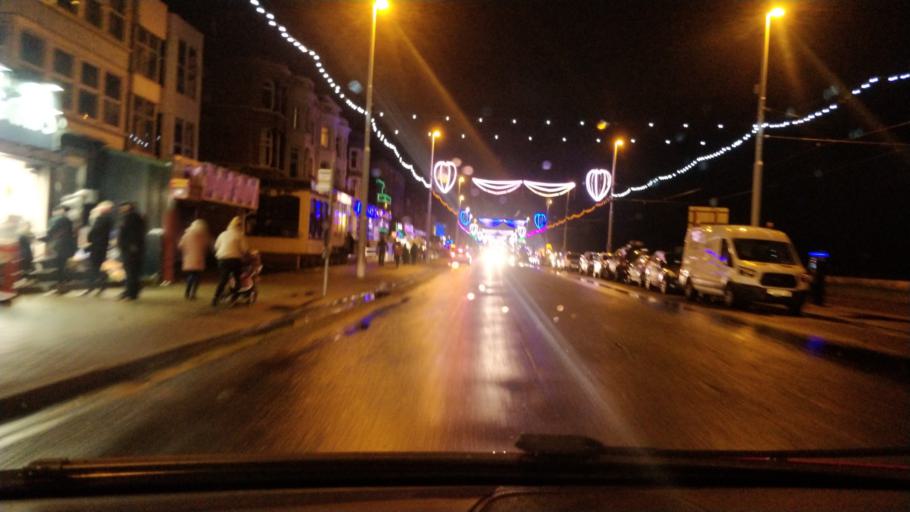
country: GB
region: England
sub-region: Blackpool
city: Blackpool
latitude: 53.8062
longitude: -3.0552
